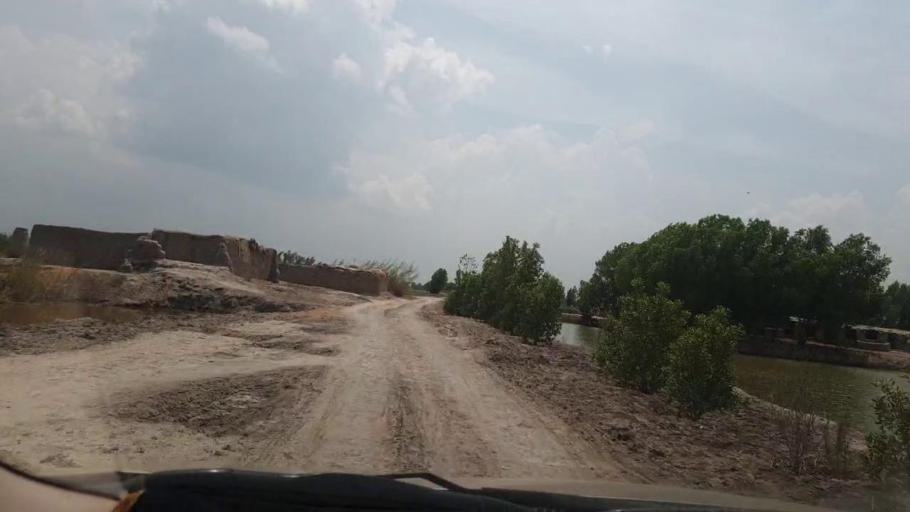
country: PK
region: Sindh
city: Larkana
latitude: 27.6164
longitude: 68.1546
